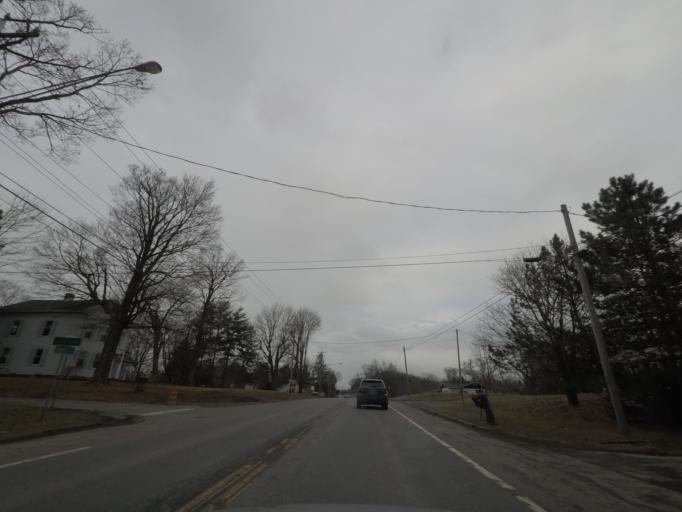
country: US
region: New York
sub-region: Madison County
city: Wampsville
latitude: 43.0747
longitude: -75.7122
